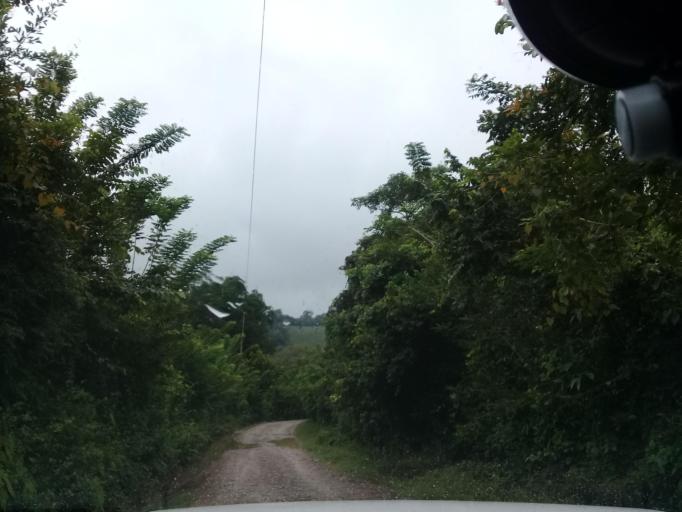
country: MX
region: Veracruz
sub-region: Chalma
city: San Pedro Coyutla
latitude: 21.2408
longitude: -98.4221
